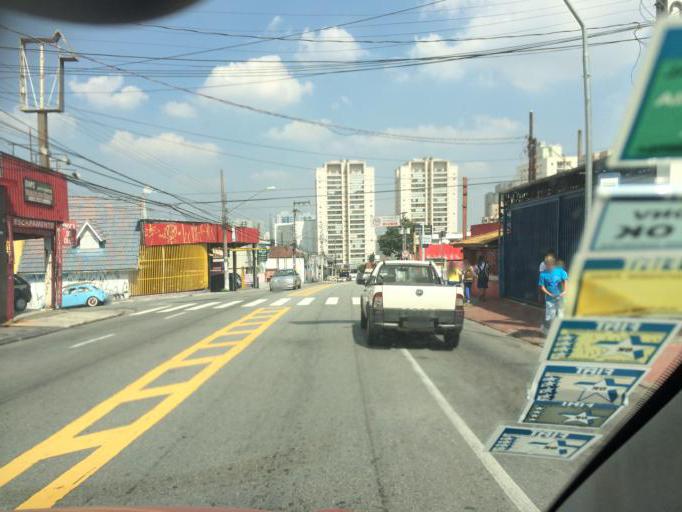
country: BR
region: Sao Paulo
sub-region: Guarulhos
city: Guarulhos
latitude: -23.4570
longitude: -46.5377
